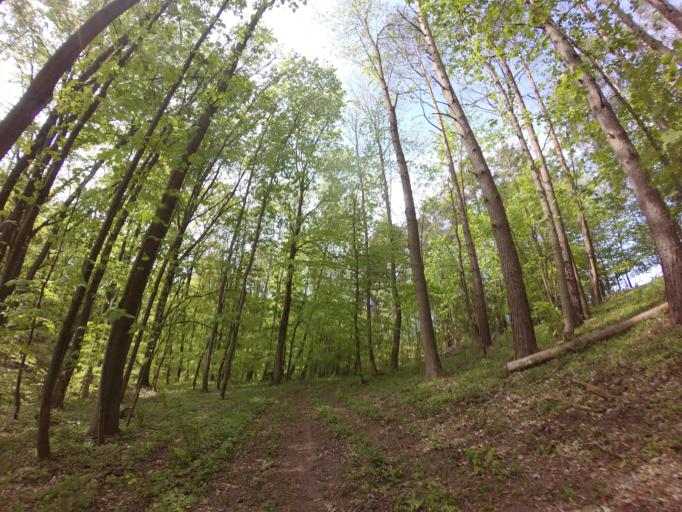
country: PL
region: West Pomeranian Voivodeship
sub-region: Powiat choszczenski
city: Choszczno
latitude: 53.2259
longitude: 15.4155
